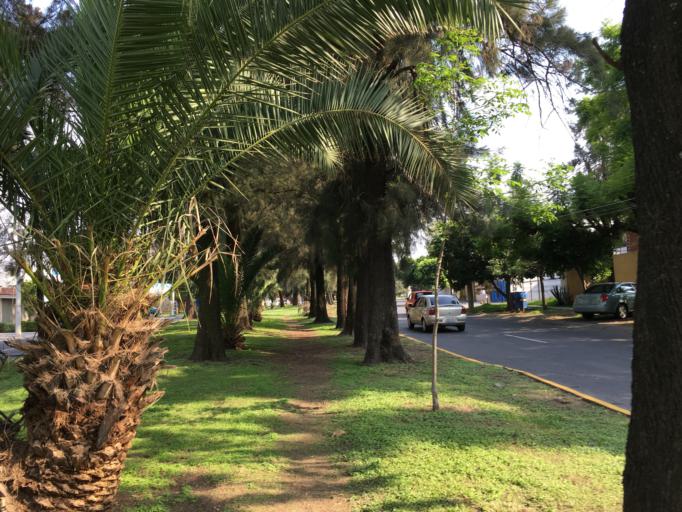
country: MX
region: Jalisco
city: Guadalajara
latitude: 20.6512
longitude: -103.3936
